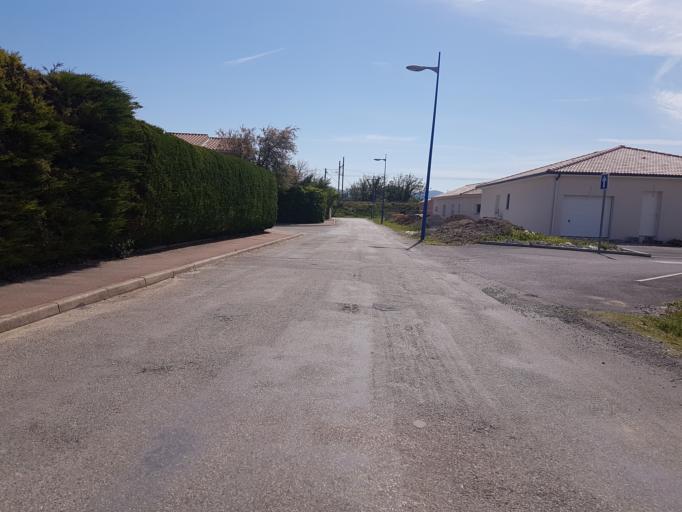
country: FR
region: Rhone-Alpes
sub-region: Departement de l'Ardeche
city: Le Pouzin
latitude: 44.7417
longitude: 4.7467
